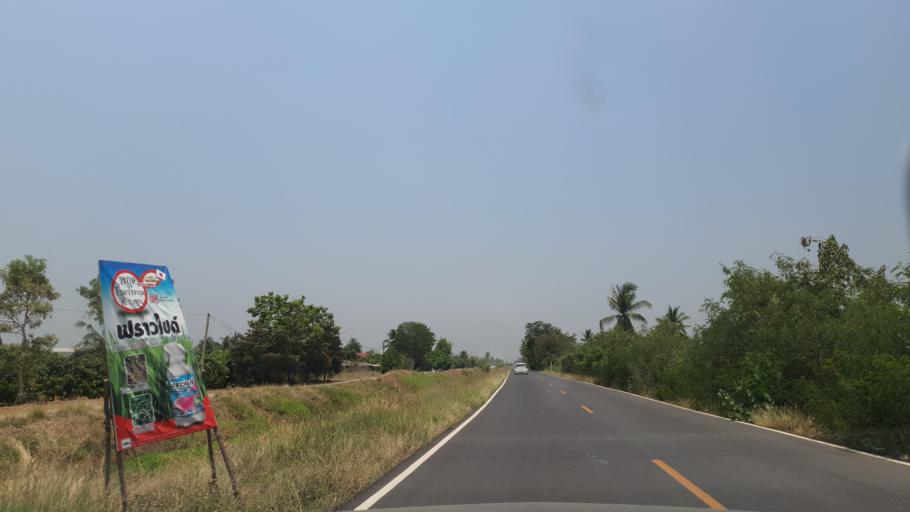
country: TH
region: Suphan Buri
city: Si Prachan
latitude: 14.6226
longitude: 100.0963
